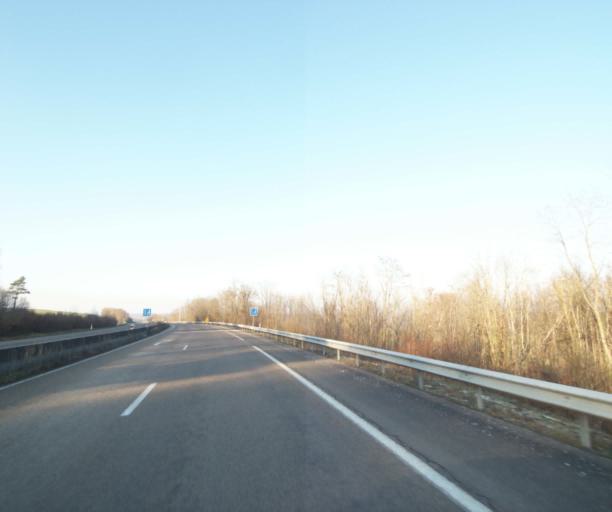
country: FR
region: Champagne-Ardenne
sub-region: Departement de la Haute-Marne
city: Chevillon
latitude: 48.5324
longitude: 5.0920
